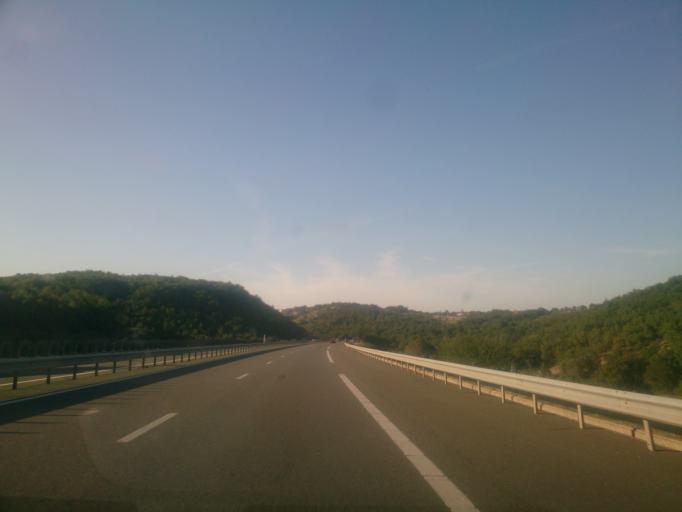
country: FR
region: Midi-Pyrenees
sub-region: Departement du Lot
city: Le Vigan
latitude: 44.7306
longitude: 1.5566
